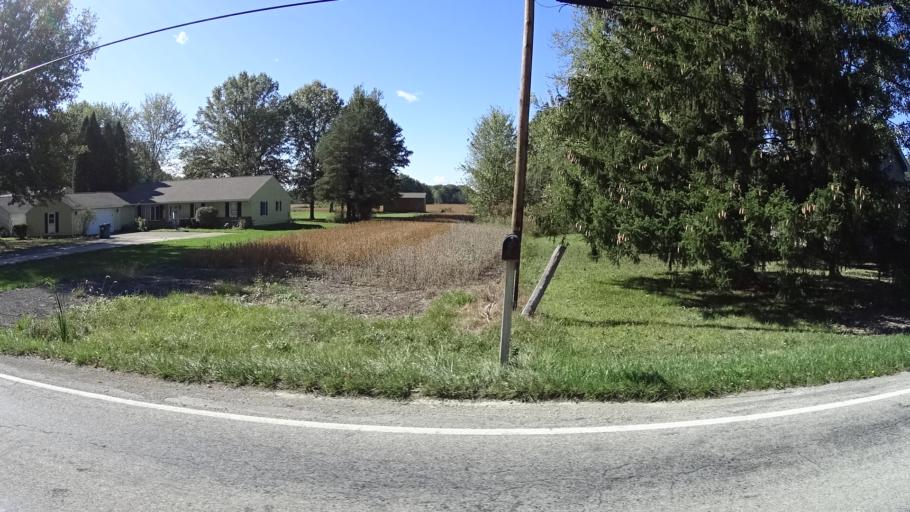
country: US
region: Ohio
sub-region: Lorain County
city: Grafton
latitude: 41.3122
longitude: -82.0901
